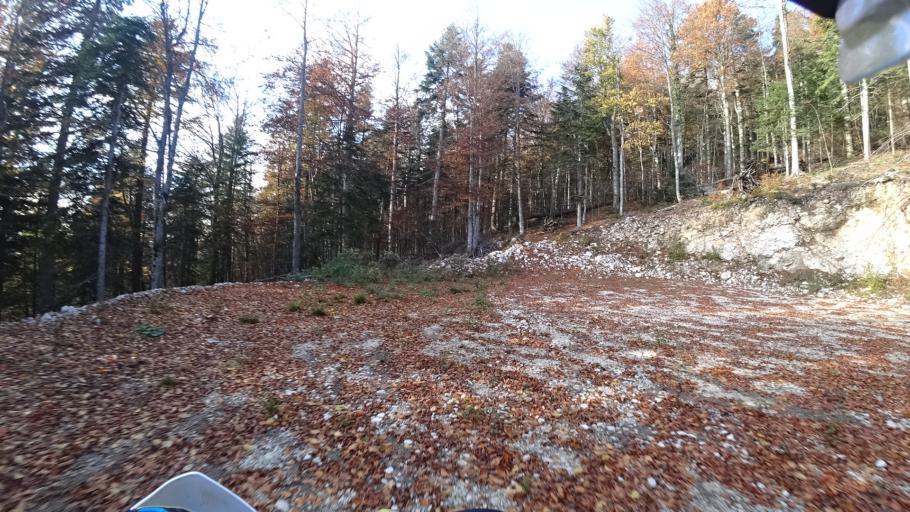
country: HR
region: Karlovacka
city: Plaski
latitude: 44.9561
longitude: 15.3966
